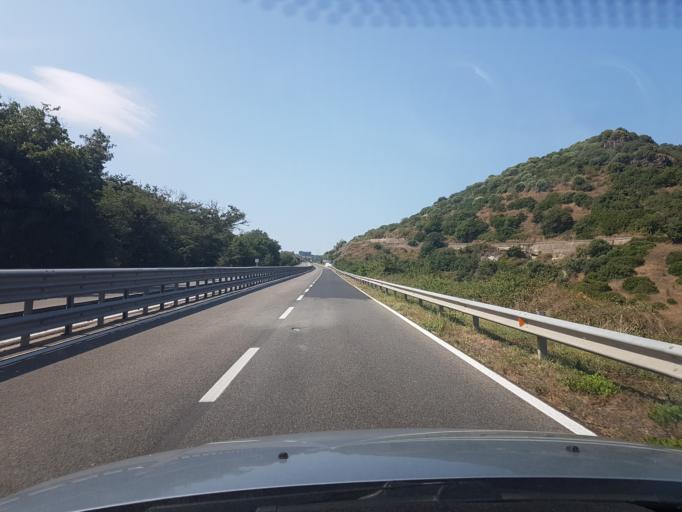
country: IT
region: Sardinia
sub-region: Provincia di Oristano
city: Soddi
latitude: 40.1421
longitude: 8.8728
